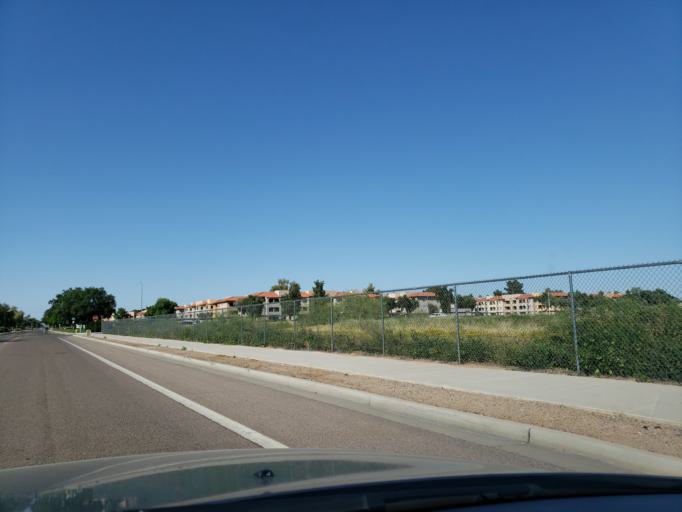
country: US
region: Arizona
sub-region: Maricopa County
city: Glendale
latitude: 33.5628
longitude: -112.1949
